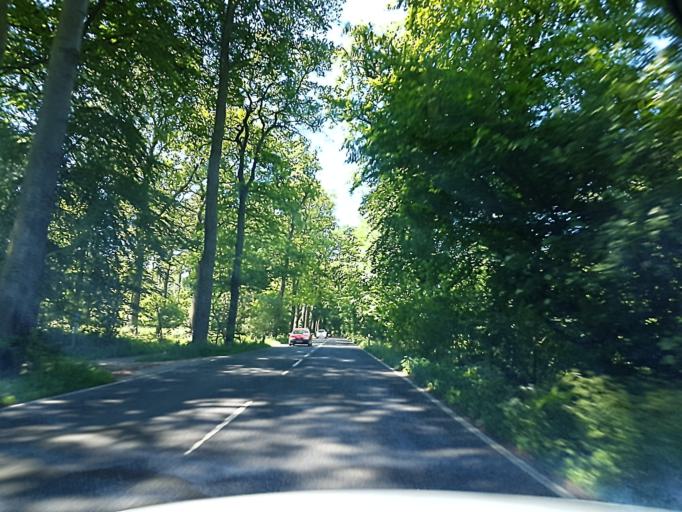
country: DE
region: North Rhine-Westphalia
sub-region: Regierungsbezirk Dusseldorf
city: Ratingen
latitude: 51.3367
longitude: 6.8038
